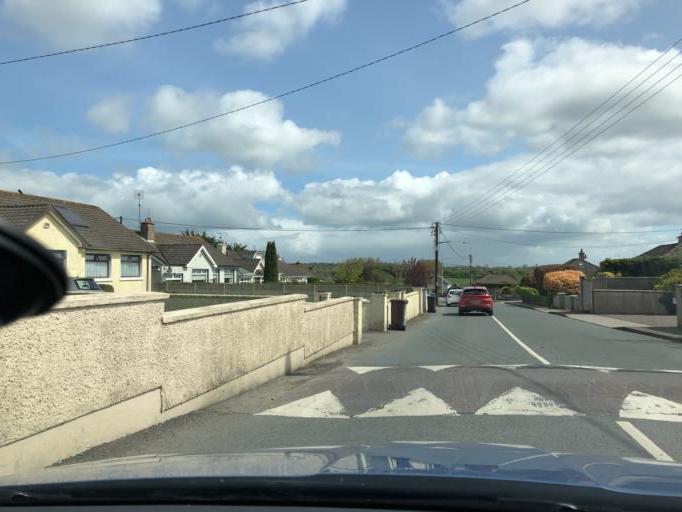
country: IE
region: Munster
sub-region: County Cork
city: Mallow
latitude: 52.1451
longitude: -8.6419
